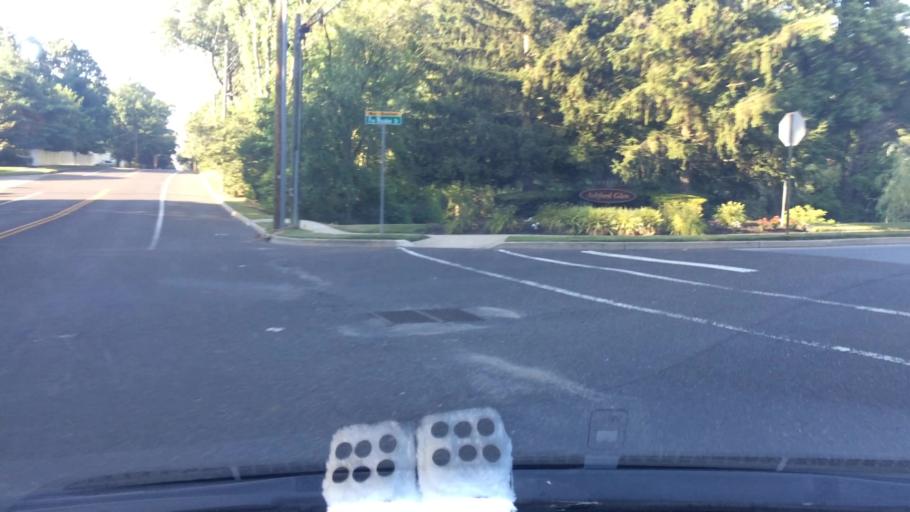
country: US
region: New Jersey
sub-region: Gloucester County
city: Turnersville
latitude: 39.7640
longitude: -75.0337
